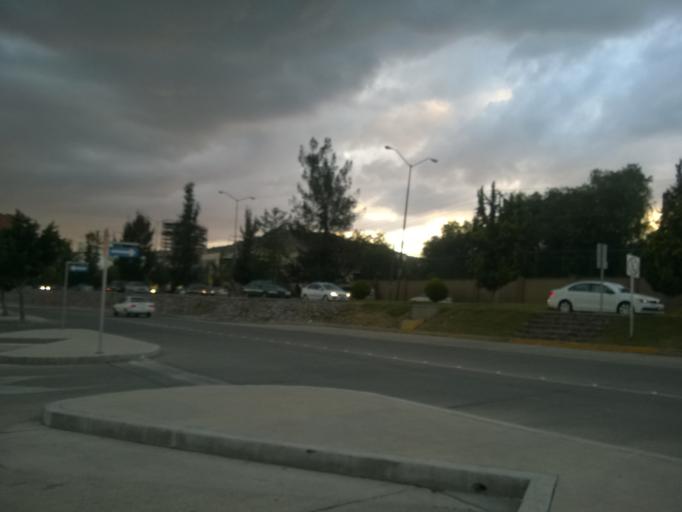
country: MX
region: Guanajuato
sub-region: Leon
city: La Ermita
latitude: 21.1598
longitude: -101.6959
